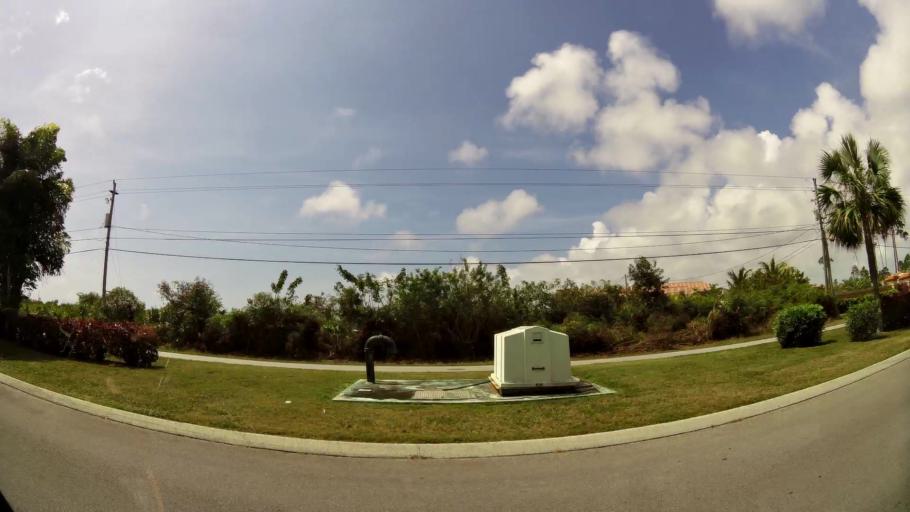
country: BS
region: Freeport
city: Freeport
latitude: 26.5092
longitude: -78.6978
